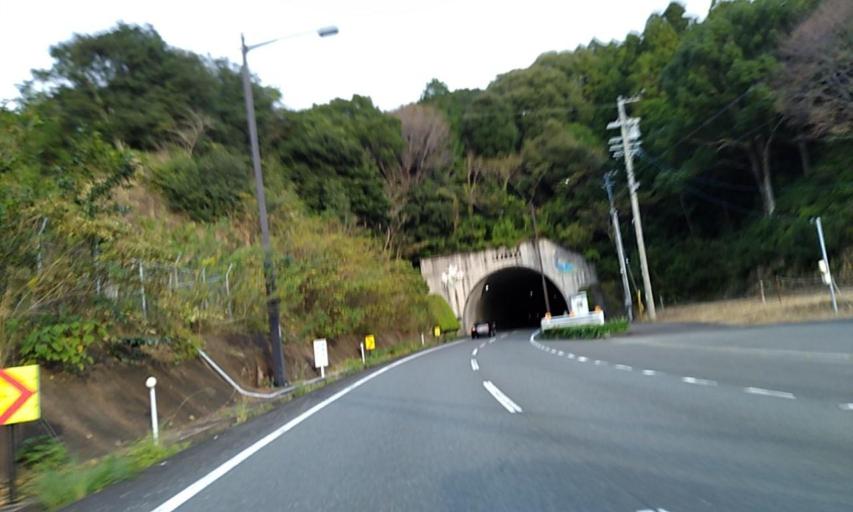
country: JP
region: Mie
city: Toba
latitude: 34.3613
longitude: 136.7963
